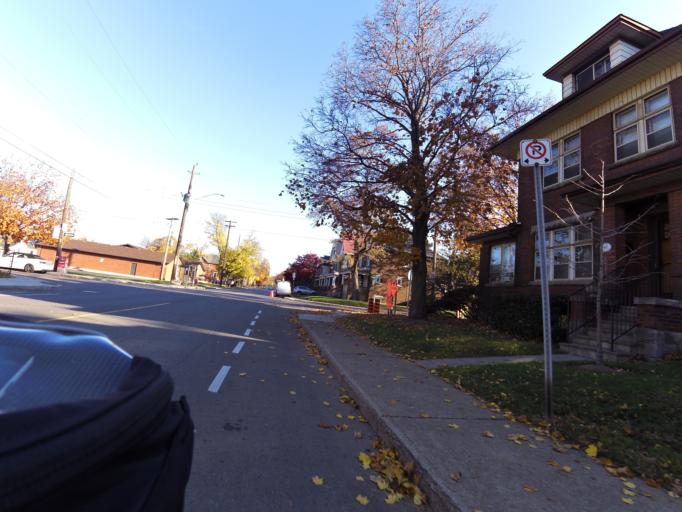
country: CA
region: Ontario
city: Hamilton
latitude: 43.2477
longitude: -79.8485
